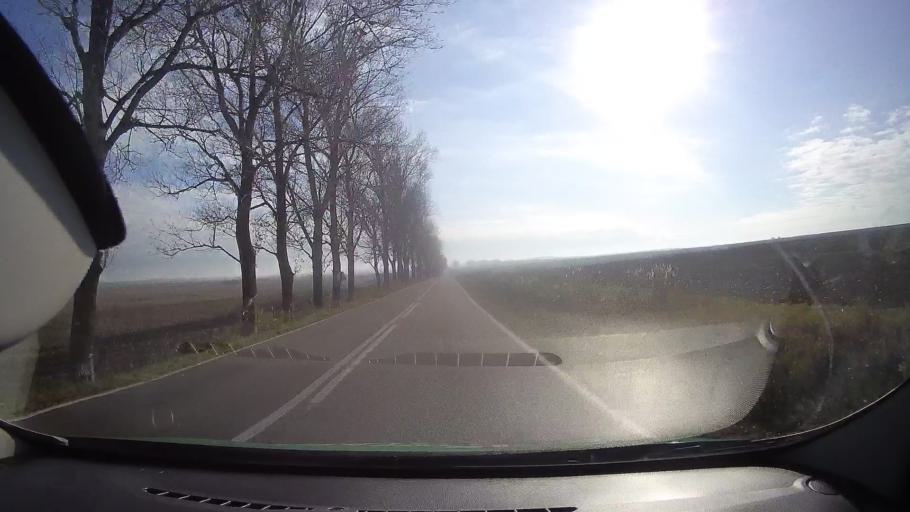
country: RO
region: Tulcea
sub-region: Comuna Mahmudia
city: Mahmudia
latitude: 45.0660
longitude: 29.1069
